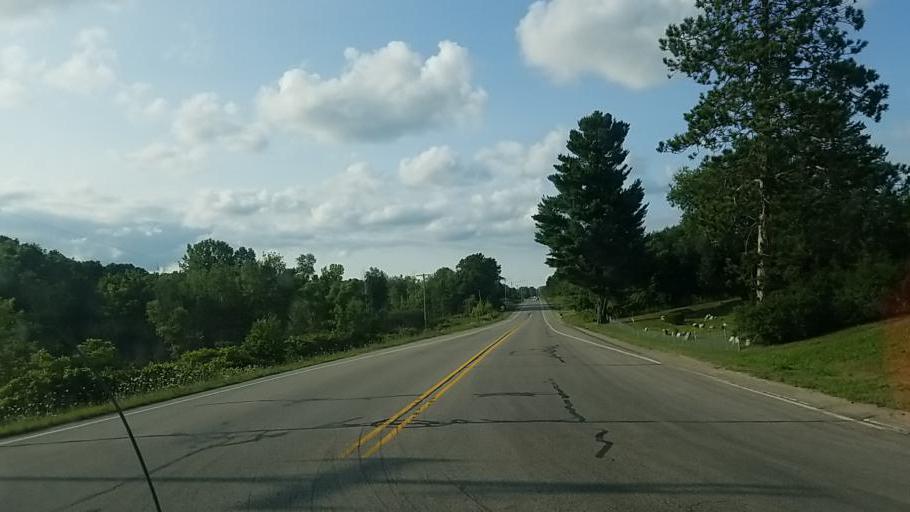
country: US
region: Michigan
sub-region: Kent County
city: Lowell
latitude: 43.0166
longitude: -85.3518
